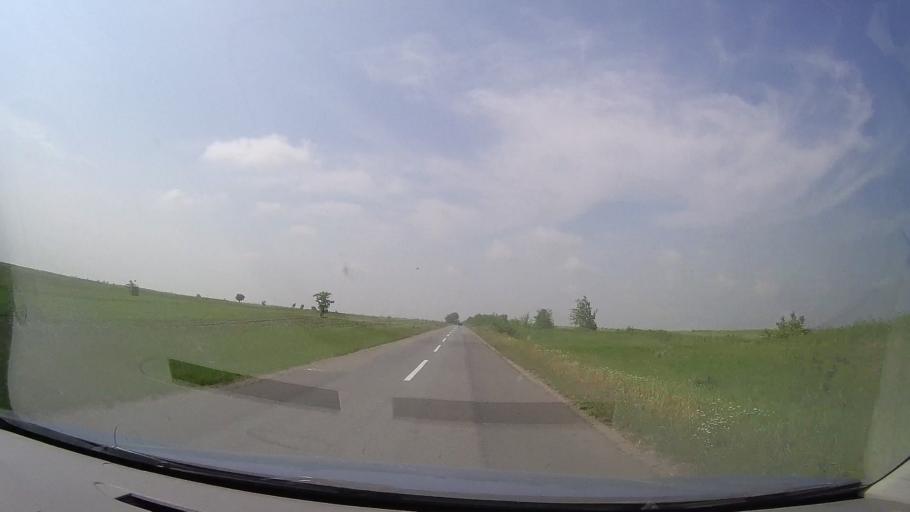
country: RS
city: Padina
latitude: 45.1485
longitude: 20.7436
